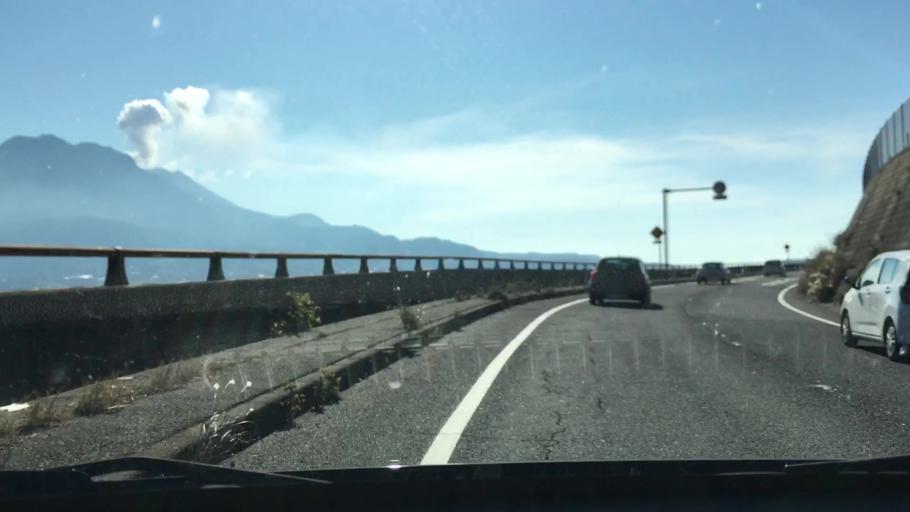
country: JP
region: Kagoshima
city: Kagoshima-shi
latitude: 31.6388
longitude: 130.6027
